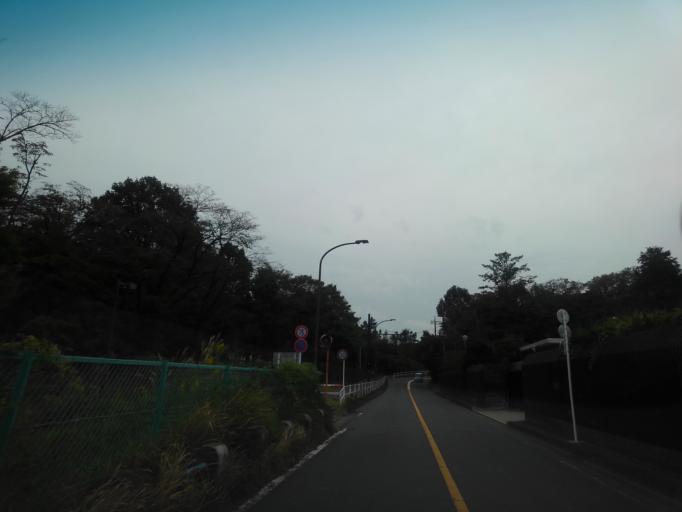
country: JP
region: Tokyo
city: Higashimurayama-shi
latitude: 35.7620
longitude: 139.4171
